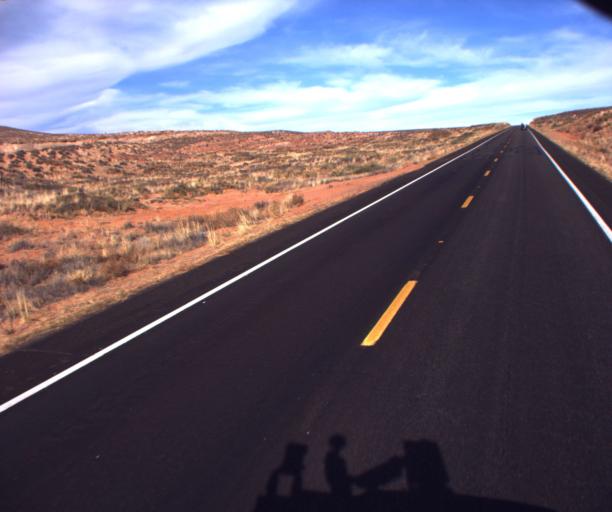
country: US
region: Arizona
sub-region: Apache County
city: Many Farms
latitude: 36.9452
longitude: -109.5330
